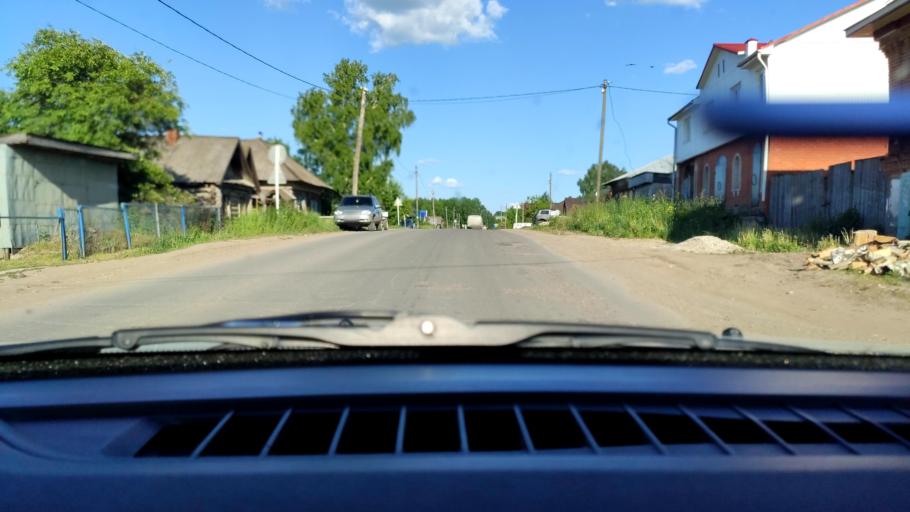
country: RU
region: Perm
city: Orda
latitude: 57.1921
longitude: 56.8994
